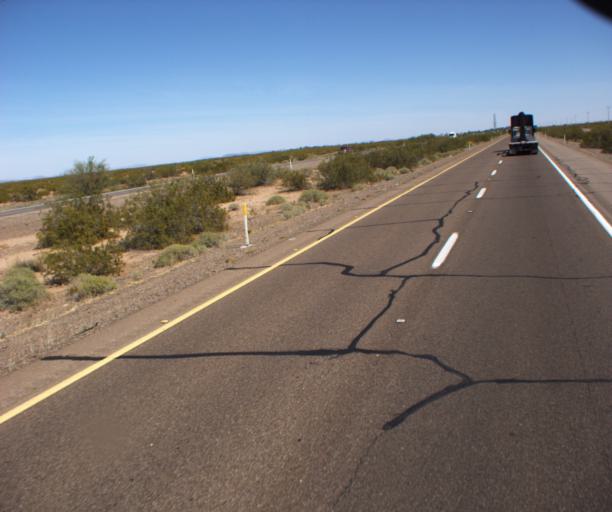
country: US
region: Arizona
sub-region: Yuma County
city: Wellton
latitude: 32.7868
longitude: -113.5666
